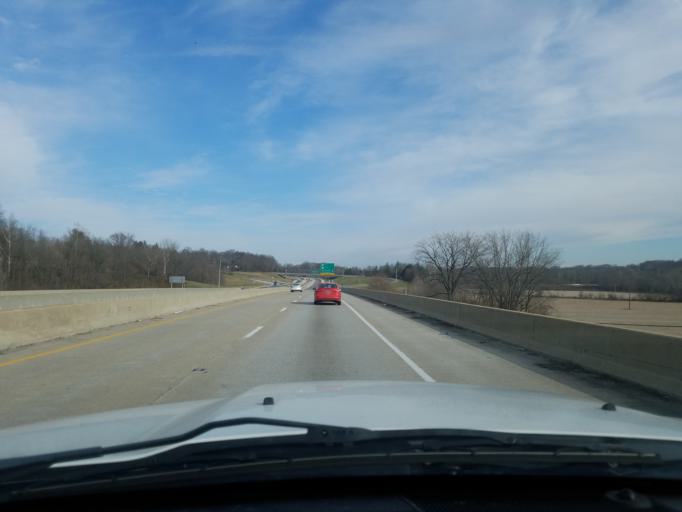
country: US
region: Indiana
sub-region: Lawrence County
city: Bedford
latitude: 38.8259
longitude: -86.5124
